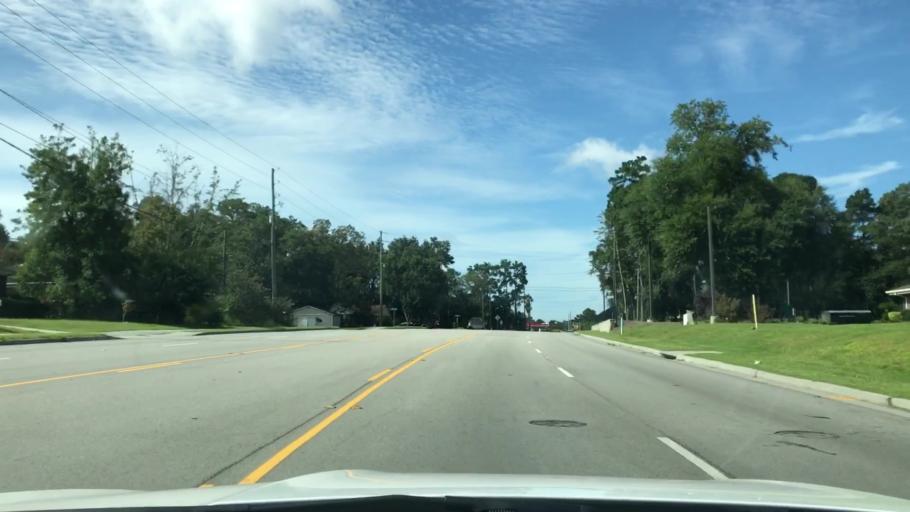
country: US
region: South Carolina
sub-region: Dorchester County
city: Centerville
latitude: 32.9706
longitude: -80.1992
